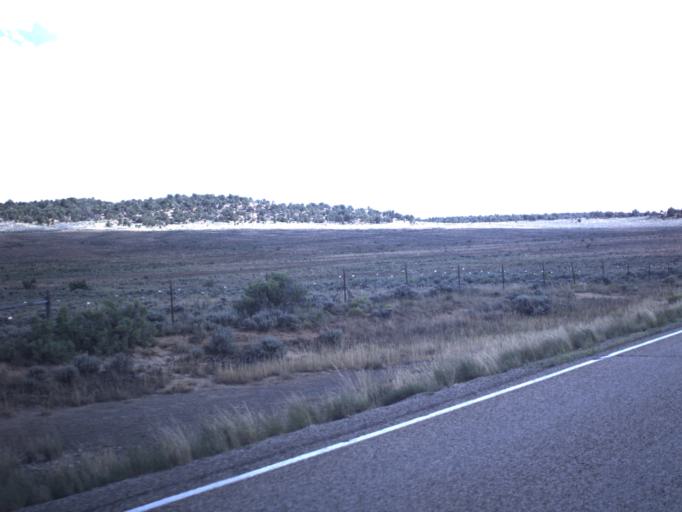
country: US
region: Utah
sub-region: Duchesne County
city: Duchesne
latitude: 40.2551
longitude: -110.7102
